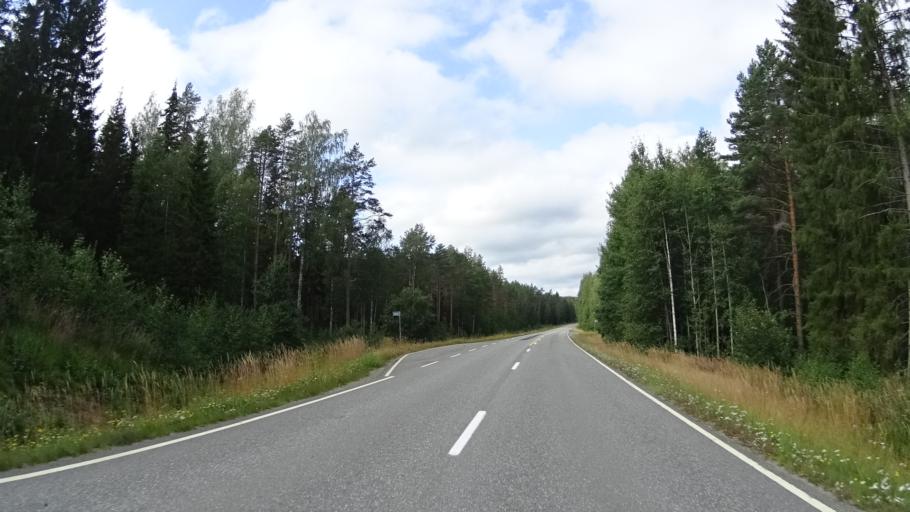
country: FI
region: Pirkanmaa
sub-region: Tampere
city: Luopioinen
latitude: 61.4971
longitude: 24.8039
